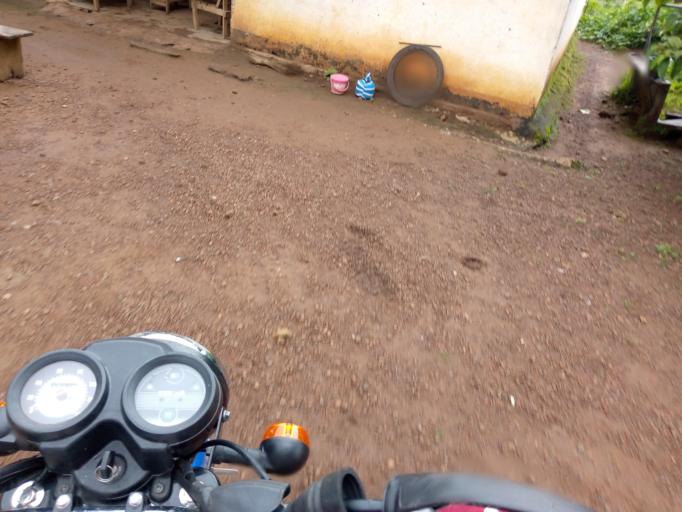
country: SL
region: Eastern Province
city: Buedu
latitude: 8.4654
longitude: -10.3401
